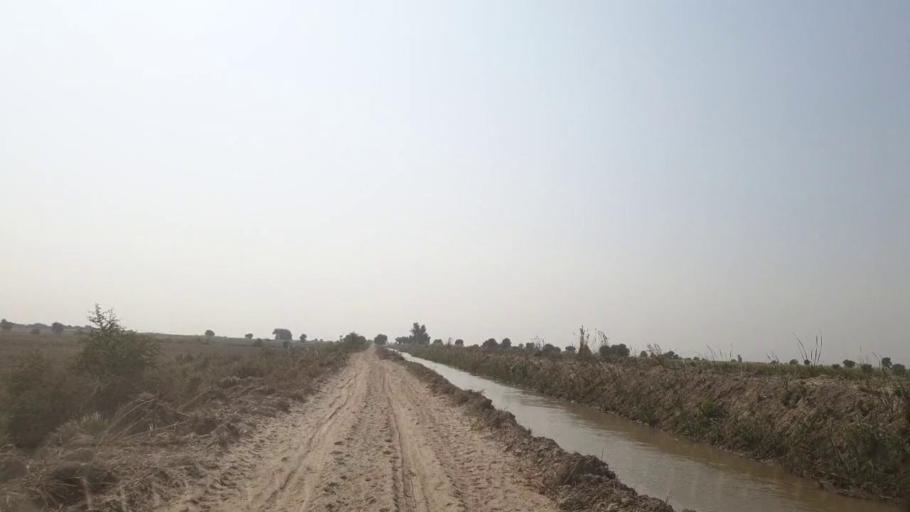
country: PK
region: Sindh
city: Bulri
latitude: 24.9788
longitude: 68.4034
